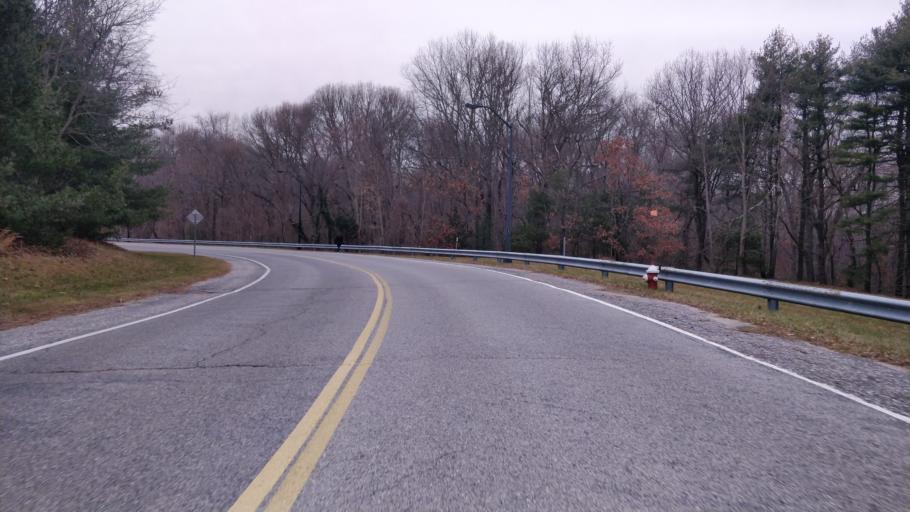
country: US
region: New York
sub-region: Nassau County
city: Brookville
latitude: 40.8030
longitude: -73.5738
